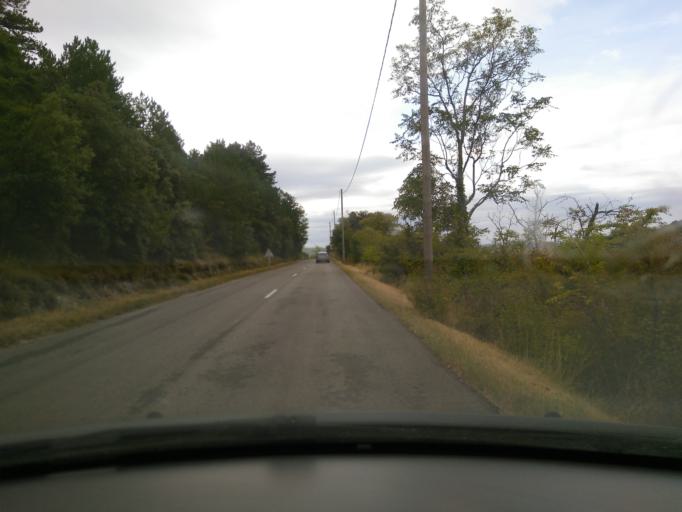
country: FR
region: Rhone-Alpes
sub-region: Departement de la Drome
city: Nyons
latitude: 44.4162
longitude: 5.0714
